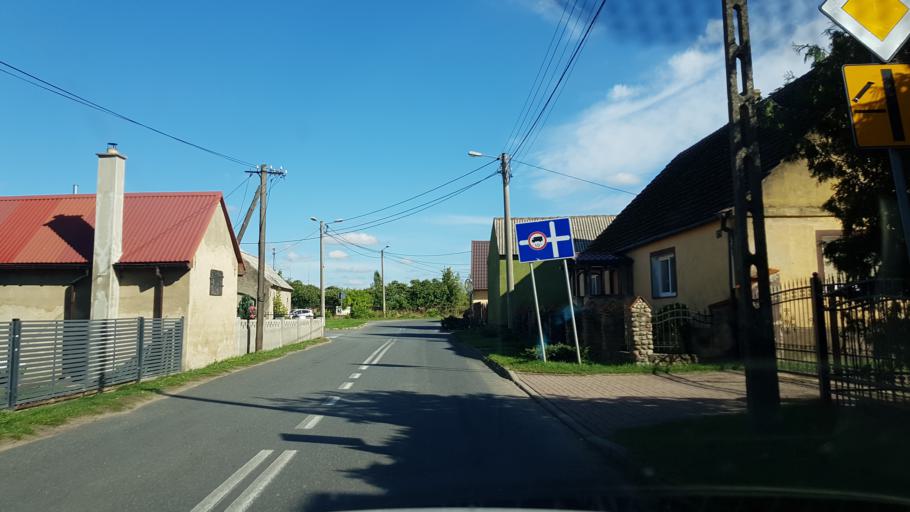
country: PL
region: West Pomeranian Voivodeship
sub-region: Powiat mysliborski
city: Nowogrodek Pomorski
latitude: 52.8806
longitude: 15.0101
